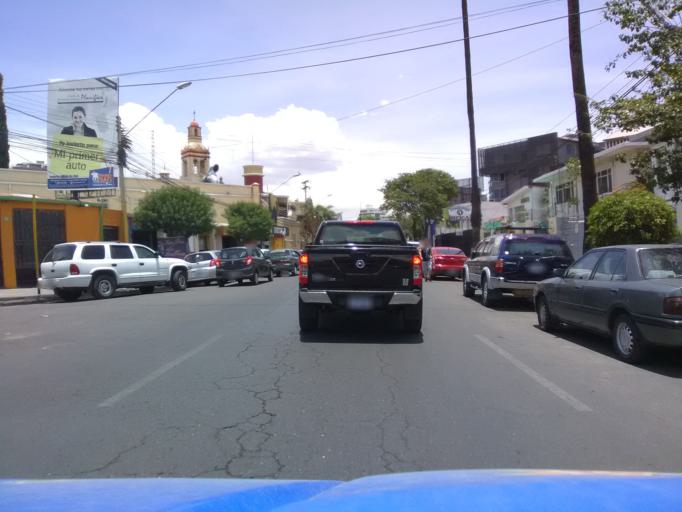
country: BO
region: Cochabamba
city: Cochabamba
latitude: -17.3775
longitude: -66.1531
